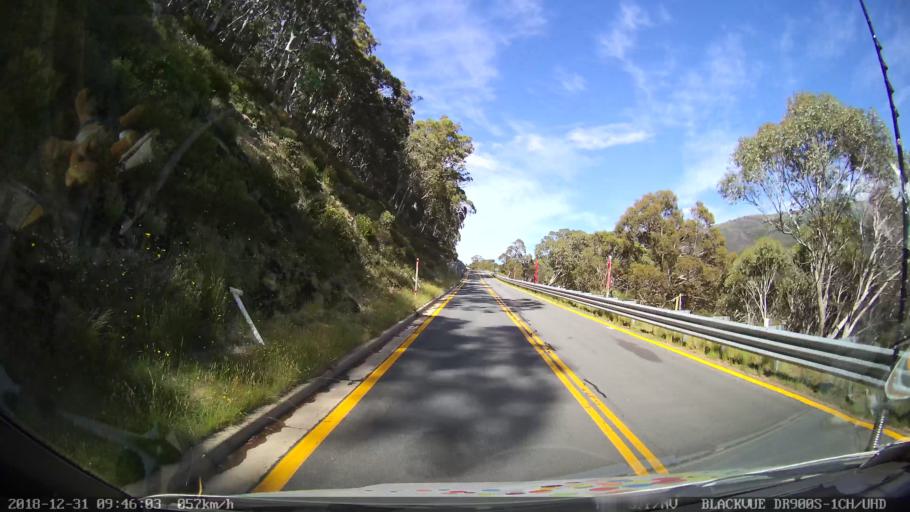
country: AU
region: New South Wales
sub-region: Snowy River
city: Jindabyne
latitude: -36.5024
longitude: 148.3128
